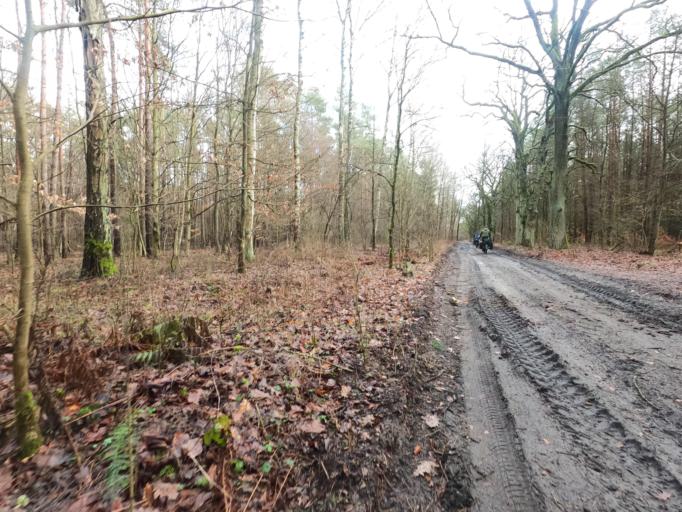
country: PL
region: Greater Poland Voivodeship
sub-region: Powiat pilski
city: Smilowo
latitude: 53.1119
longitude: 16.9382
